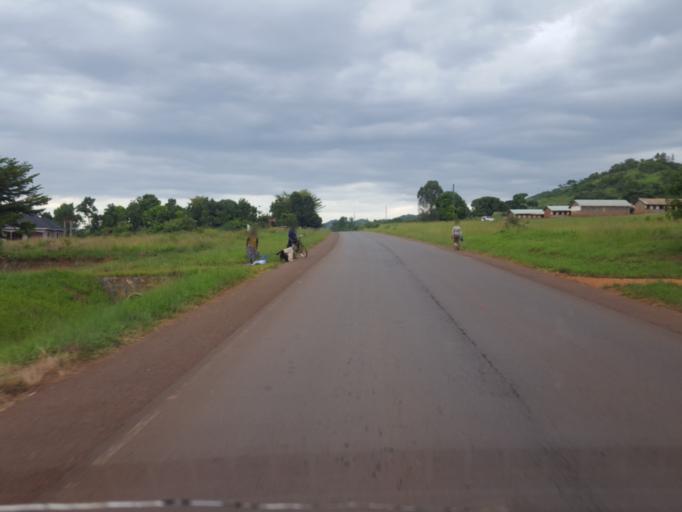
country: UG
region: Central Region
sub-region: Kiboga District
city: Kiboga
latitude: 0.8651
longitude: 31.8585
